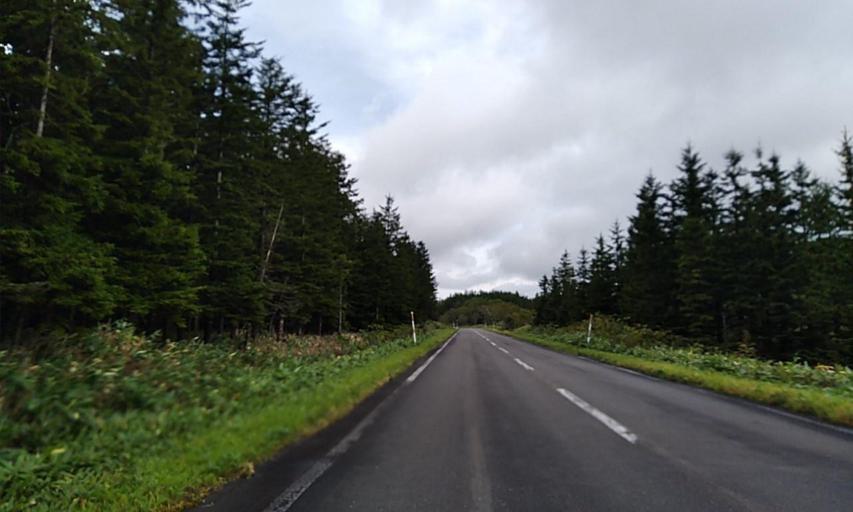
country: JP
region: Hokkaido
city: Abashiri
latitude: 43.6101
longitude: 144.5923
